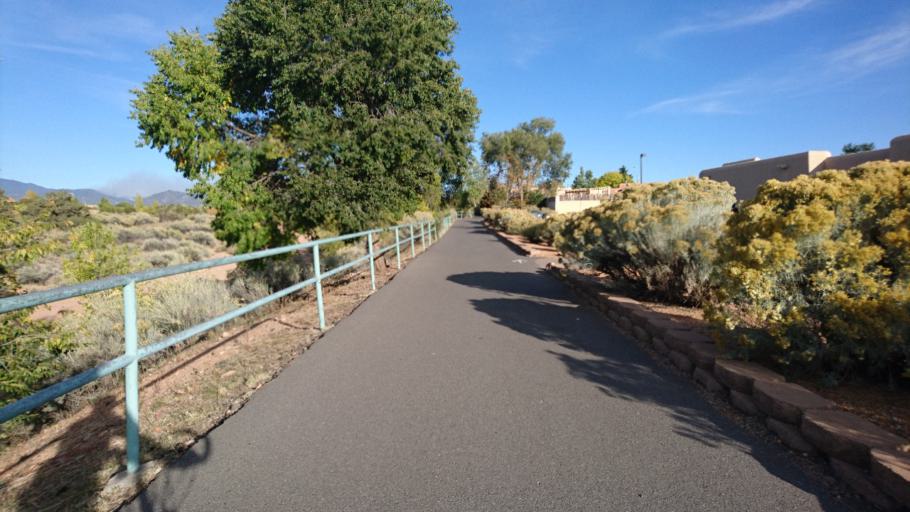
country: US
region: New Mexico
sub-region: Santa Fe County
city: Agua Fria
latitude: 35.6415
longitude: -106.0057
